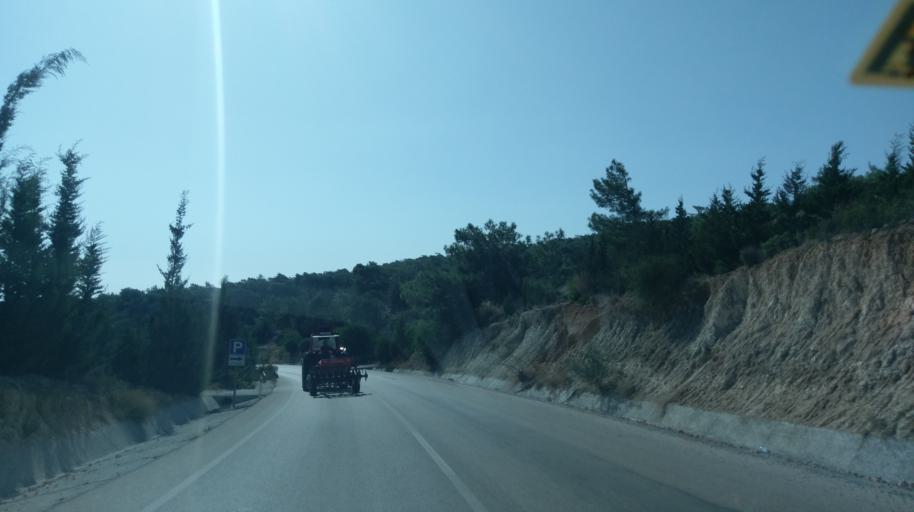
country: CY
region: Ammochostos
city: Trikomo
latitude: 35.4255
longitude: 33.9785
